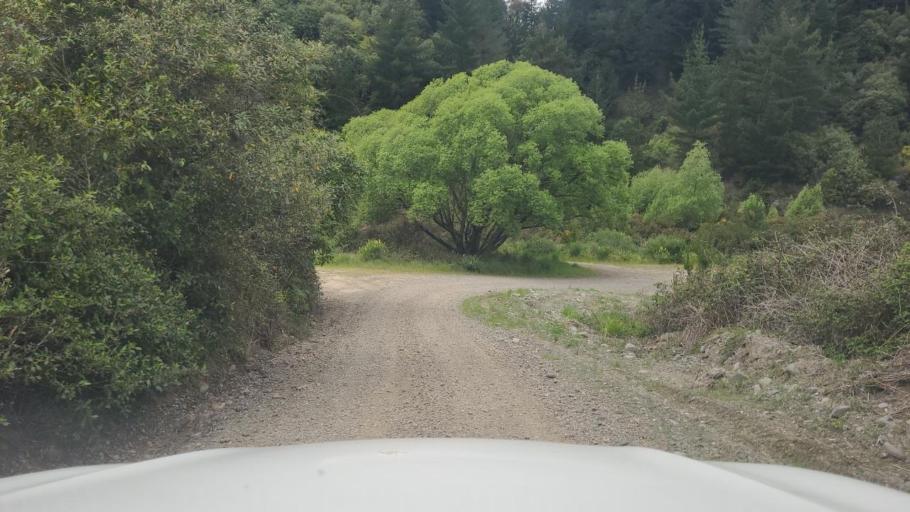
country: NZ
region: Hawke's Bay
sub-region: Napier City
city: Taradale
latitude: -39.1851
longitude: 176.6340
